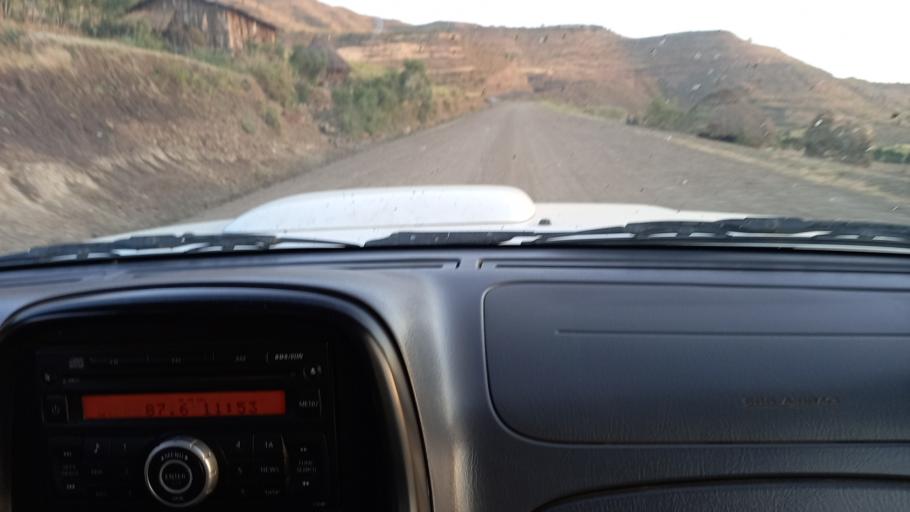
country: ET
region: Amhara
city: Debark'
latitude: 13.0550
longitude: 38.0183
